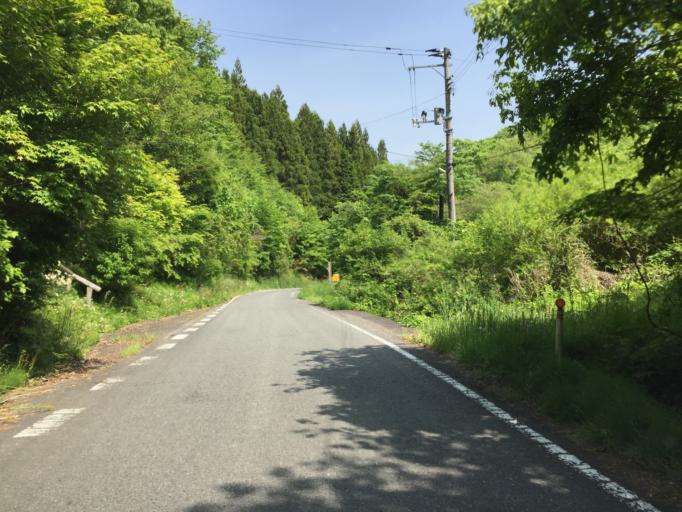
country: JP
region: Fukushima
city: Ishikawa
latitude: 37.0026
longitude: 140.6037
